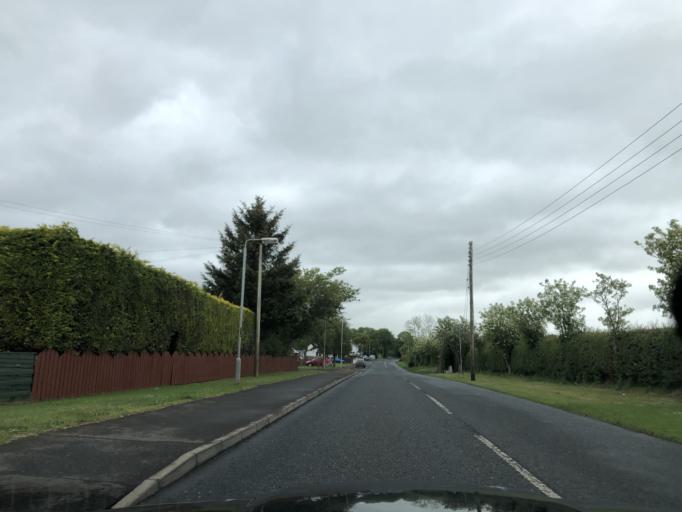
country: GB
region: Northern Ireland
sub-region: Ballymoney District
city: Ballymoney
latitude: 55.0856
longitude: -6.5098
